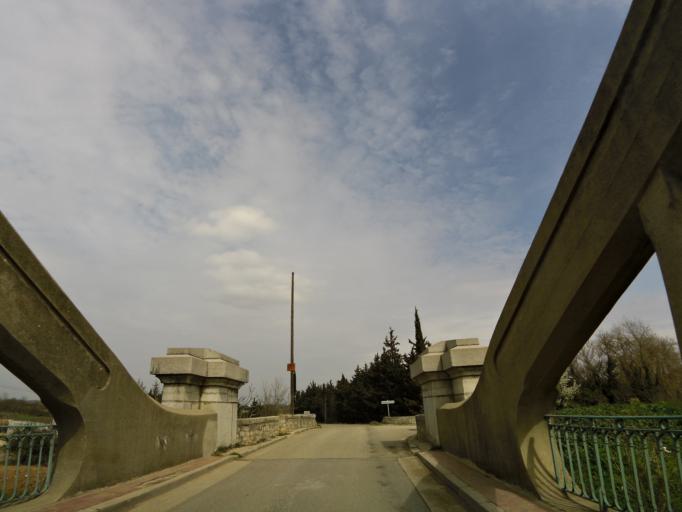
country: FR
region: Languedoc-Roussillon
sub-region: Departement de l'Herault
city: Marsillargues
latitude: 43.6674
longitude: 4.1832
